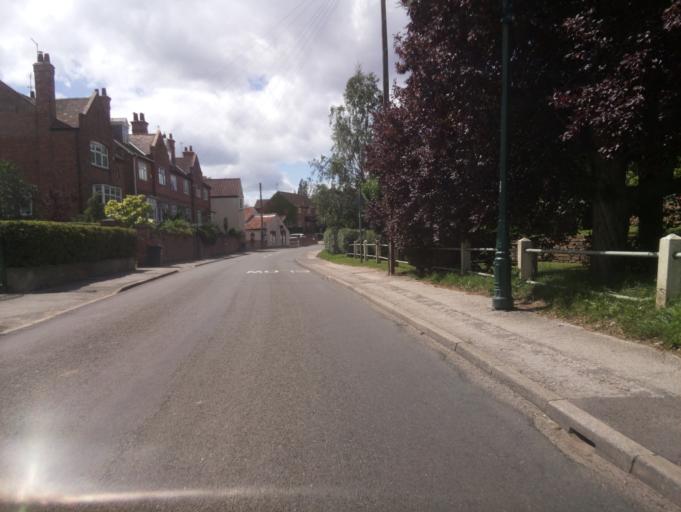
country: GB
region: England
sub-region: Nottinghamshire
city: Burton Joyce
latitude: 53.0008
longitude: -1.0619
